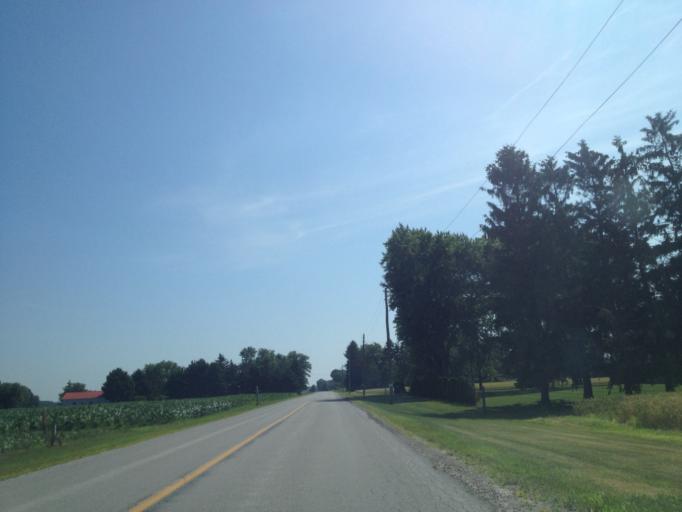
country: CA
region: Ontario
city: London
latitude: 43.1270
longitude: -81.2177
